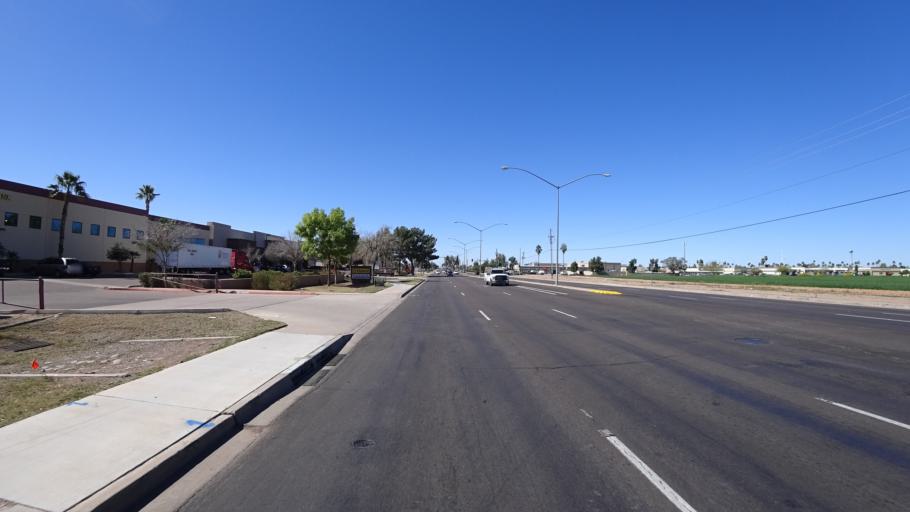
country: US
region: Arizona
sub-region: Maricopa County
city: Gilbert
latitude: 33.3788
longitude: -111.8171
